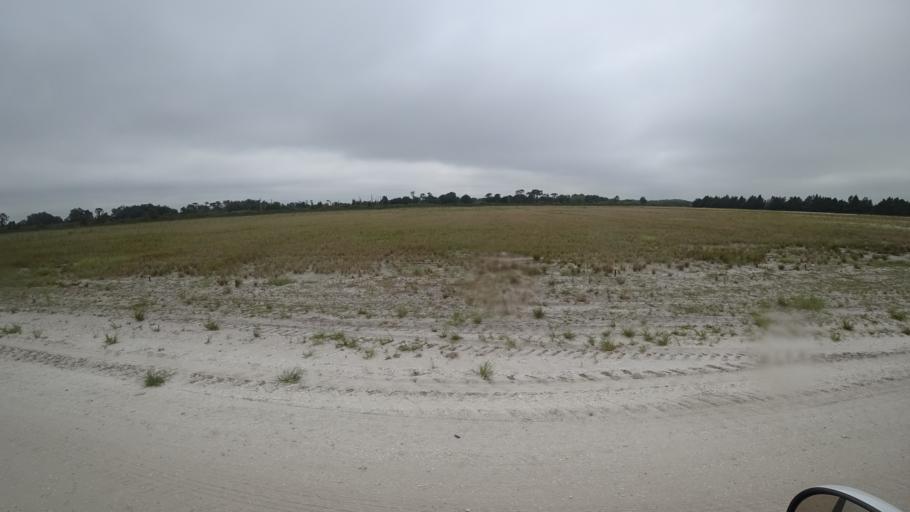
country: US
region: Florida
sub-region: Sarasota County
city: Warm Mineral Springs
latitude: 27.3012
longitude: -82.1449
